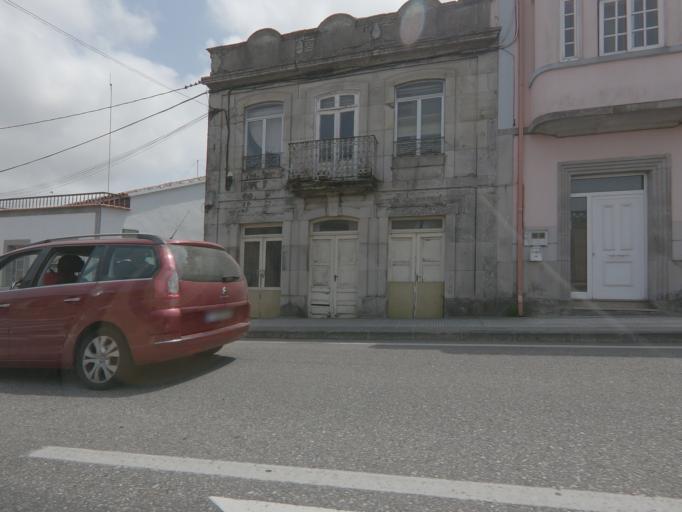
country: ES
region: Galicia
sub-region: Provincia de Pontevedra
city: A Guarda
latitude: 41.9083
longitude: -8.8598
